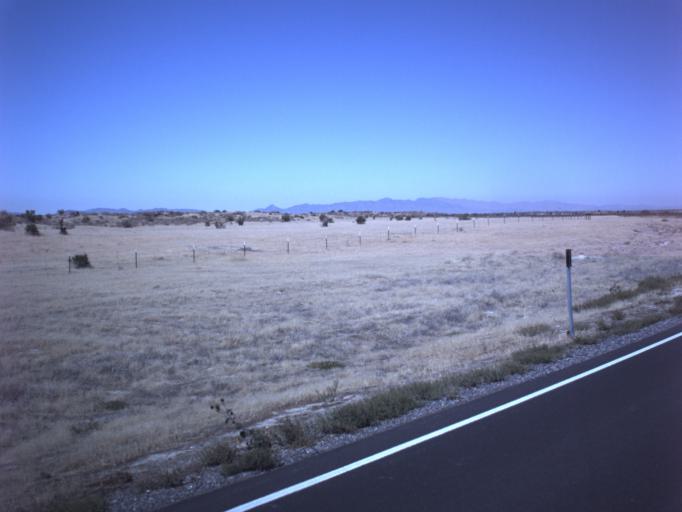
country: US
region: Utah
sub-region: Tooele County
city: Grantsville
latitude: 40.2444
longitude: -112.7231
